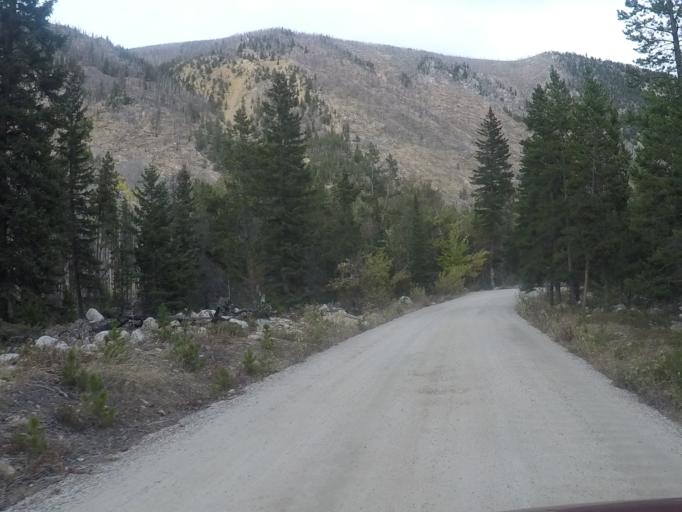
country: US
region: Montana
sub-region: Carbon County
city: Red Lodge
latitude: 45.1645
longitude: -109.3993
